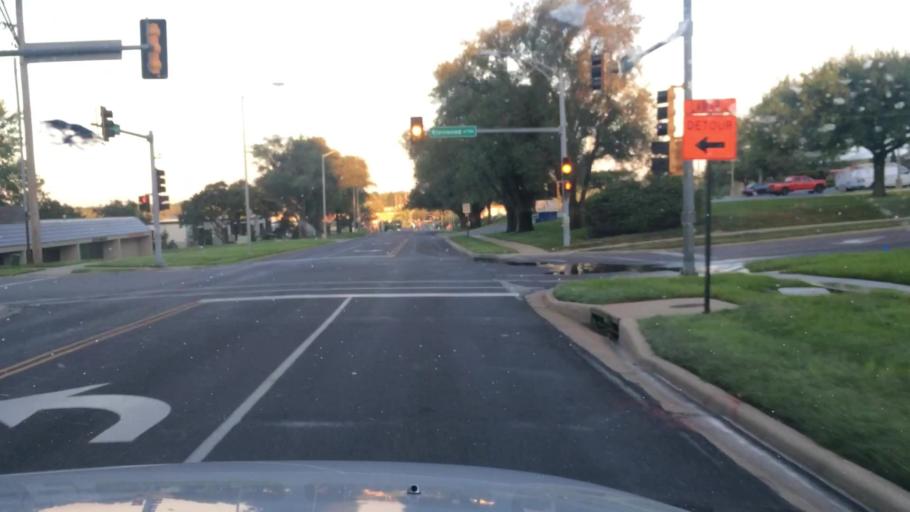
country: US
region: Kansas
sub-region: Johnson County
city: Overland Park
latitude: 38.9641
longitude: -94.6624
